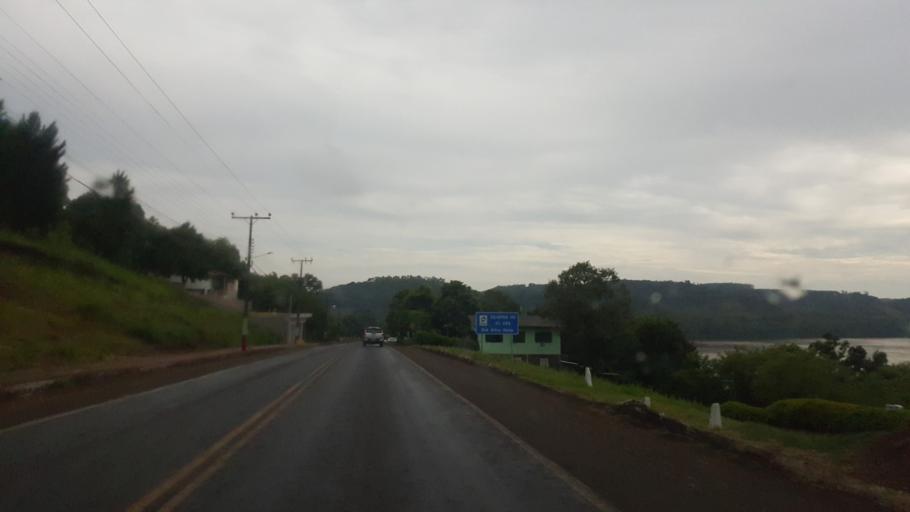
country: BR
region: Rio Grande do Sul
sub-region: Frederico Westphalen
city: Frederico Westphalen
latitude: -27.0963
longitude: -53.3876
